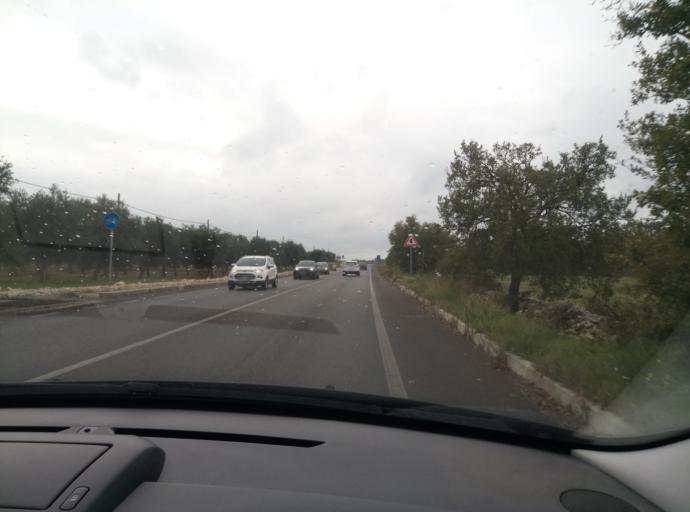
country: IT
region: Apulia
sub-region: Provincia di Bari
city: Acquaviva delle Fonti
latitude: 40.8754
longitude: 16.8085
